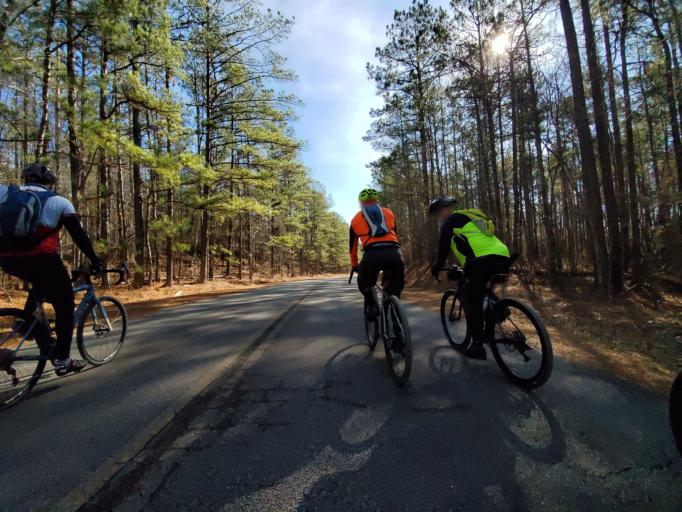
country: US
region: Georgia
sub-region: Fulton County
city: Chattahoochee Hills
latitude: 33.5738
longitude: -84.7744
